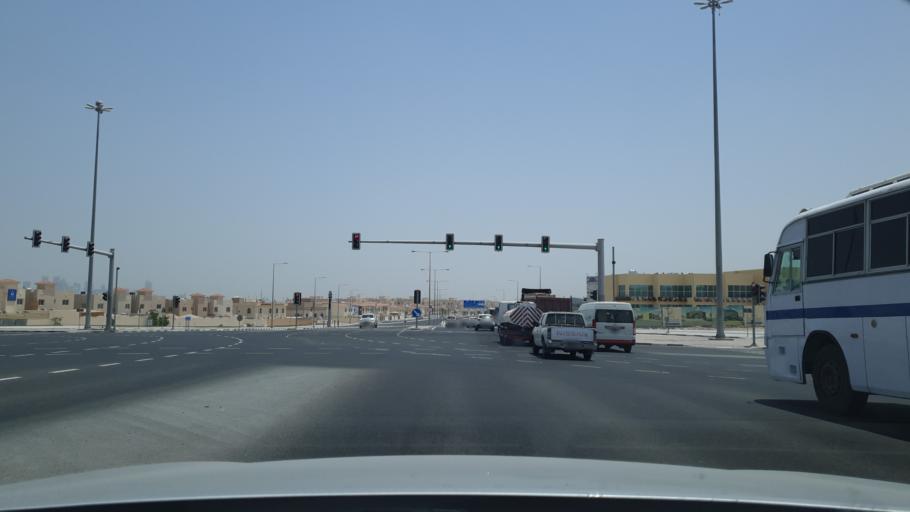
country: QA
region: Baladiyat ar Rayyan
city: Ar Rayyan
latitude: 25.3584
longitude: 51.4773
